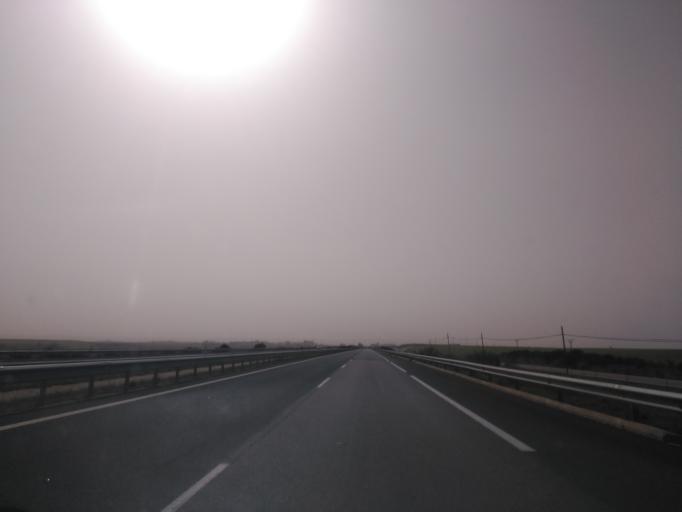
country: ES
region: Castille and Leon
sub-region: Provincia de Palencia
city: Marcilla de Campos
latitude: 42.2921
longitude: -4.3998
